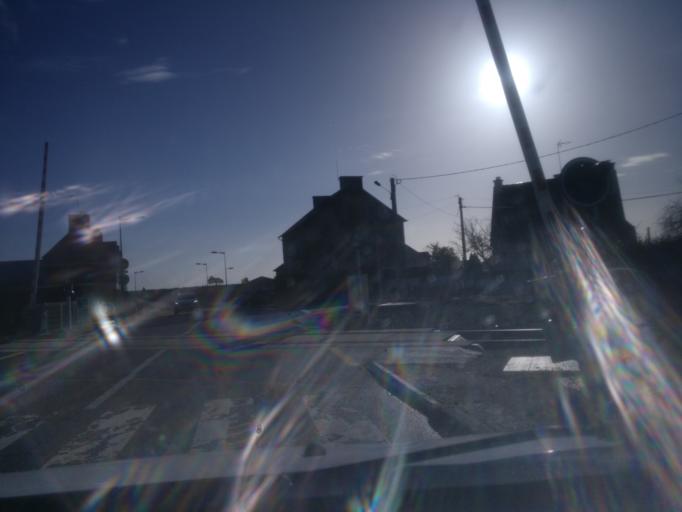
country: FR
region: Brittany
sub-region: Departement d'Ille-et-Vilaine
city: Pleine-Fougeres
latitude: 48.5335
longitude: -1.5600
